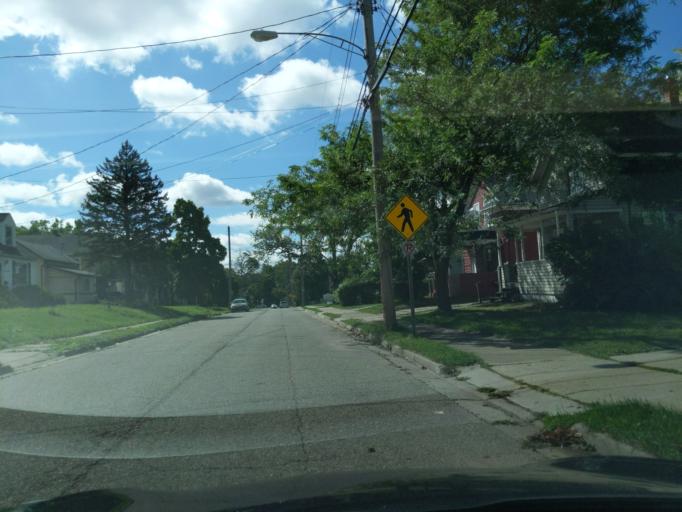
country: US
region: Michigan
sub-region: Ingham County
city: Lansing
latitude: 42.7494
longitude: -84.5359
